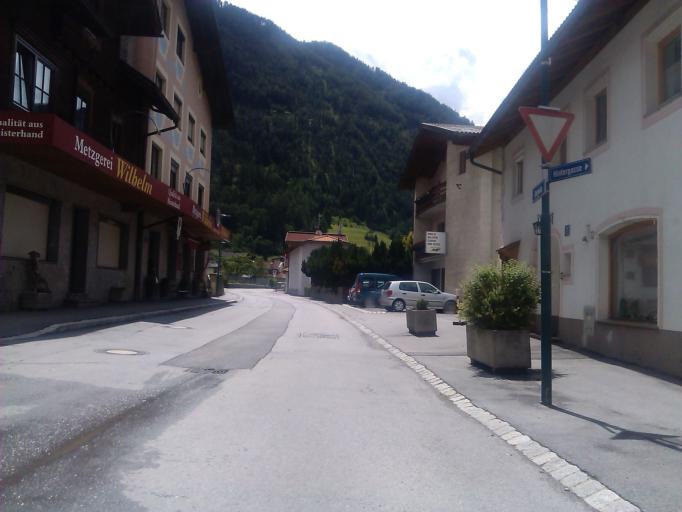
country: AT
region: Tyrol
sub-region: Politischer Bezirk Landeck
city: Prutz
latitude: 47.0750
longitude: 10.6644
